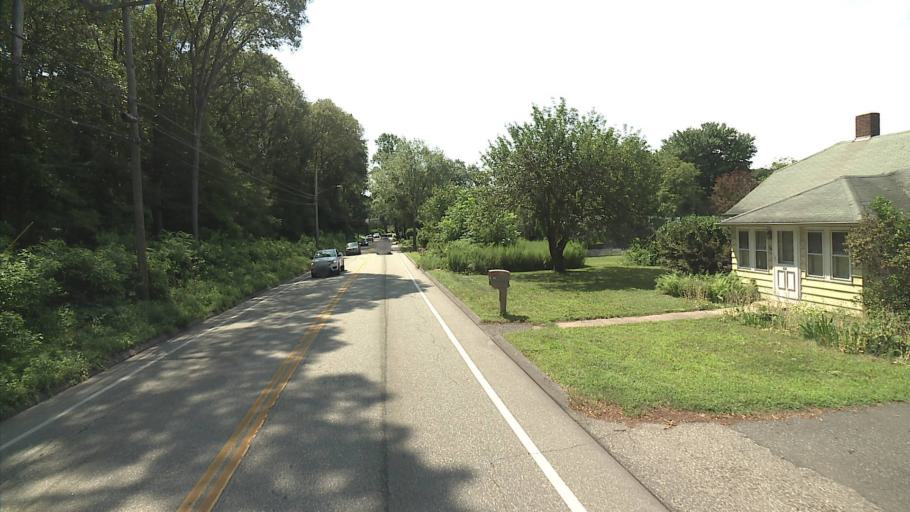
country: US
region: Connecticut
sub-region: New London County
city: Niantic
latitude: 41.3406
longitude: -72.2077
